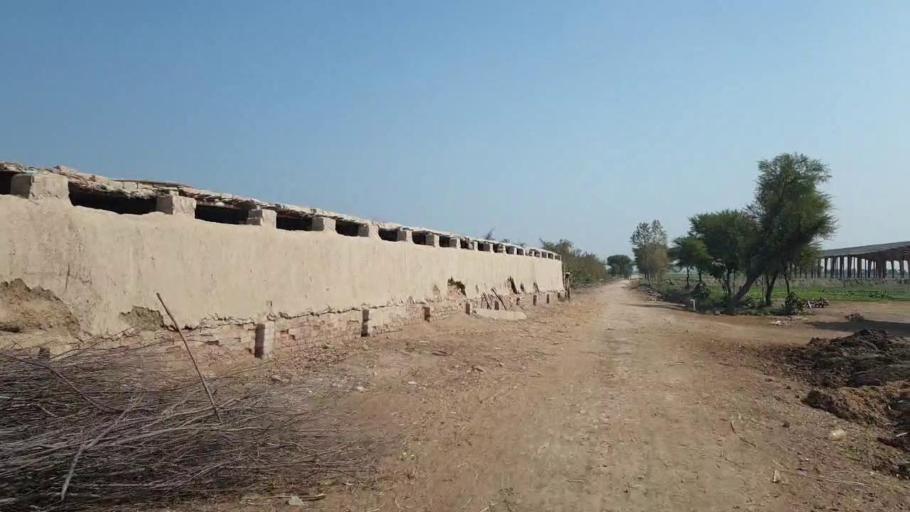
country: PK
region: Sindh
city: Hala
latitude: 25.9553
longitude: 68.4274
